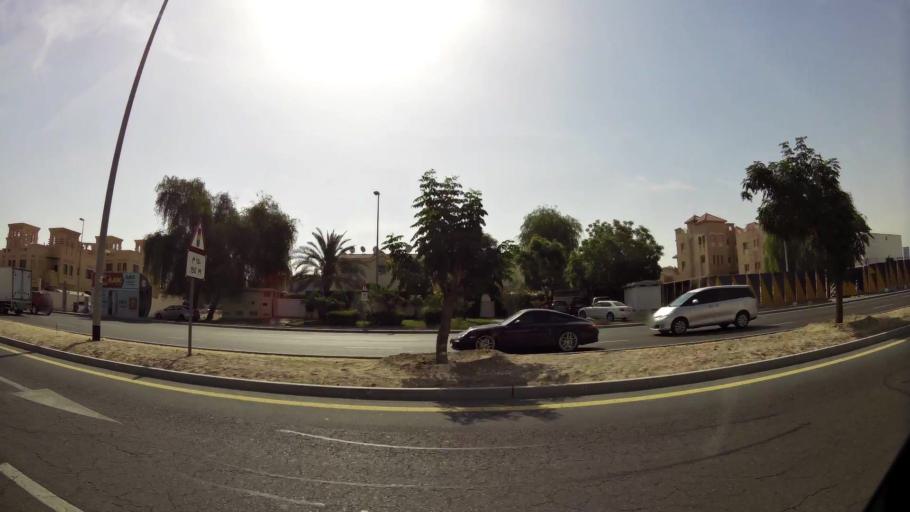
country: AE
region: Ash Shariqah
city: Sharjah
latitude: 25.2278
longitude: 55.4251
